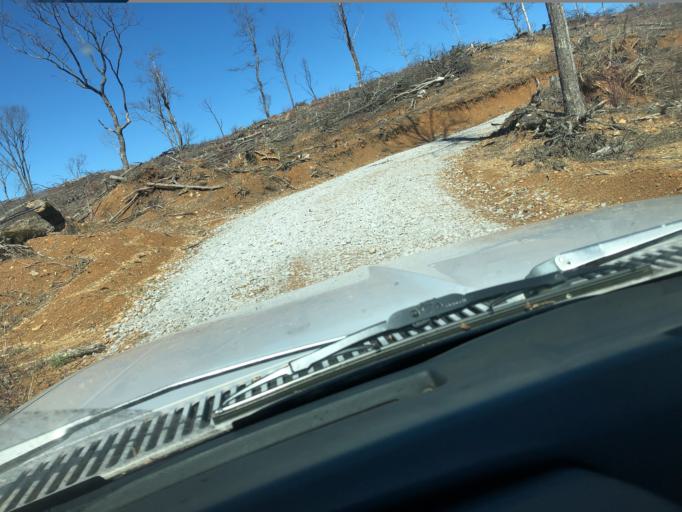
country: US
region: Tennessee
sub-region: Cumberland County
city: Fairfield Glade
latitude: 35.9732
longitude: -84.7666
